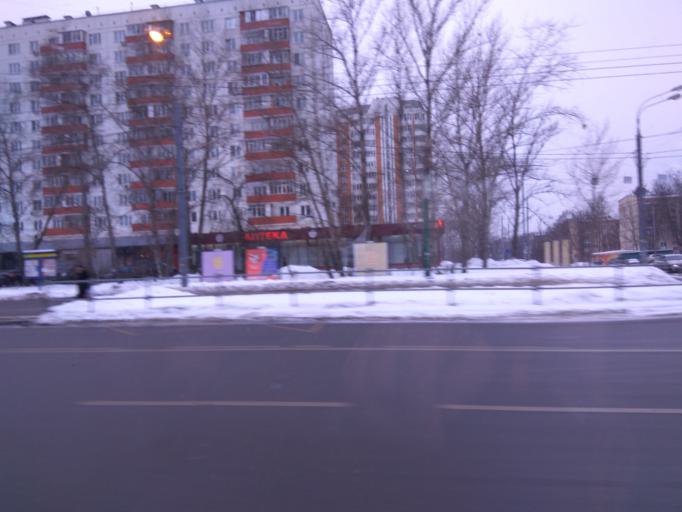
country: RU
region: Moscow
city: Metrogorodok
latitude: 55.8131
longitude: 37.7984
